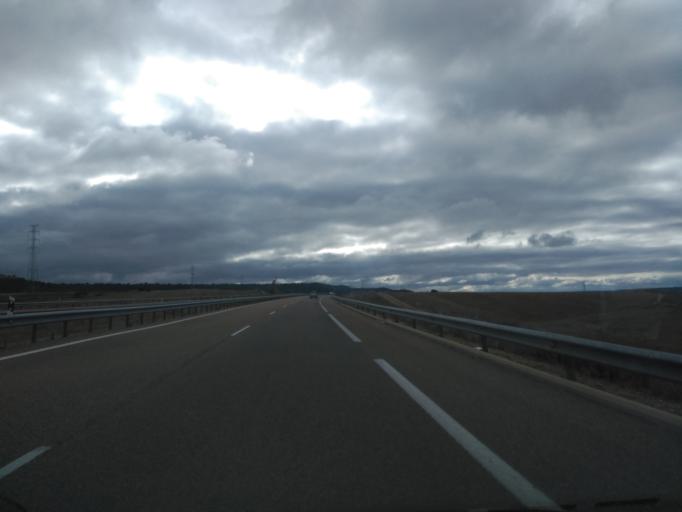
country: ES
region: Castille and Leon
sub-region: Provincia de Palencia
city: Villalobon
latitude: 42.0428
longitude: -4.4899
